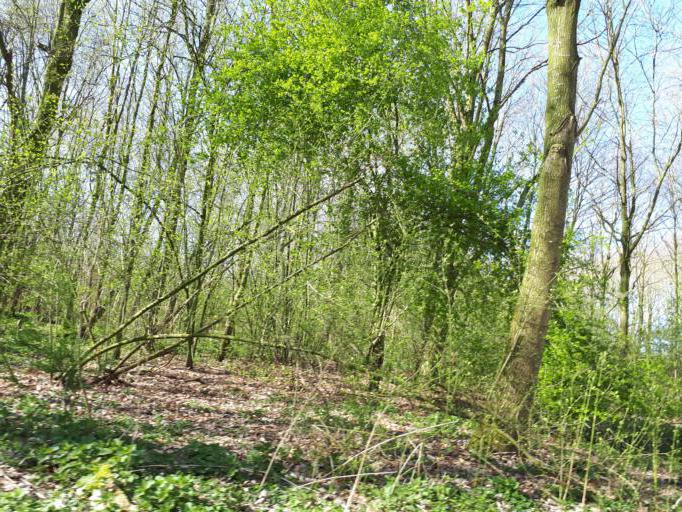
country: NL
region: South Holland
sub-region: Gemeente Pijnacker-Nootdorp
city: Pijnacker
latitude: 52.0404
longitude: 4.4565
